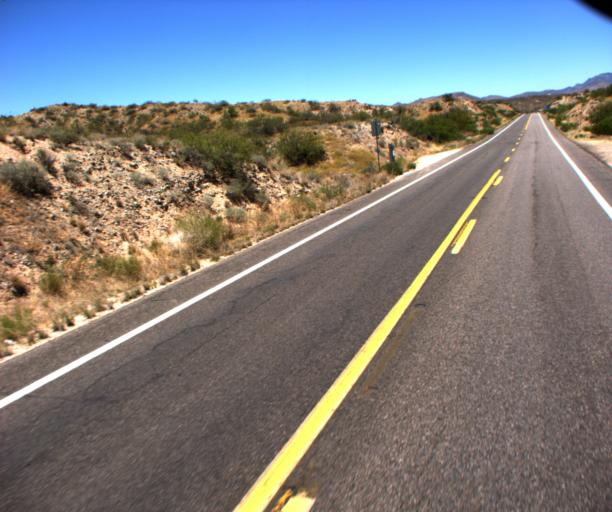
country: US
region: Arizona
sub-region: Gila County
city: Globe
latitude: 33.3601
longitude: -110.7359
